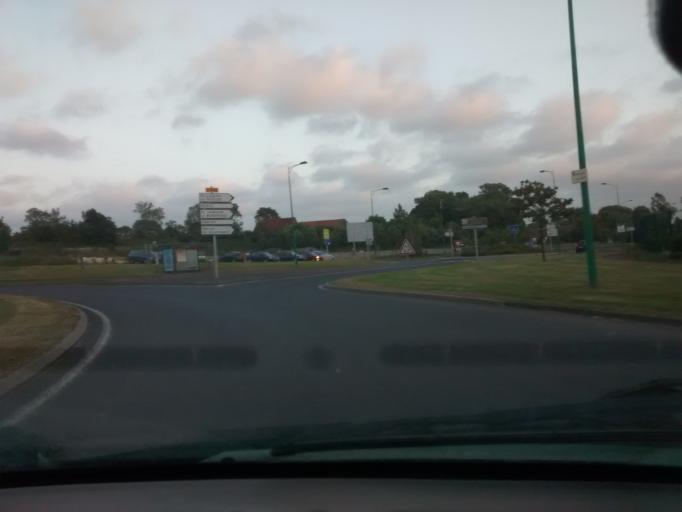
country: FR
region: Lower Normandy
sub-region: Departement de la Manche
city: Agneaux
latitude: 49.1014
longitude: -1.1166
